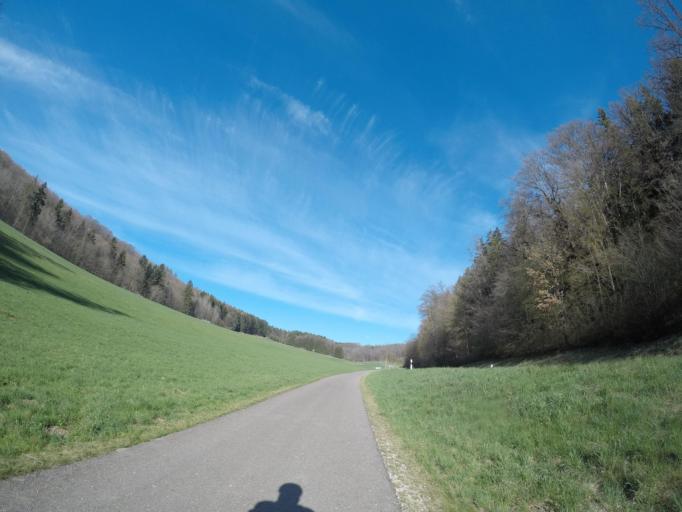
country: DE
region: Baden-Wuerttemberg
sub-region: Tuebingen Region
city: Allmendingen
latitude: 48.3451
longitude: 9.6975
